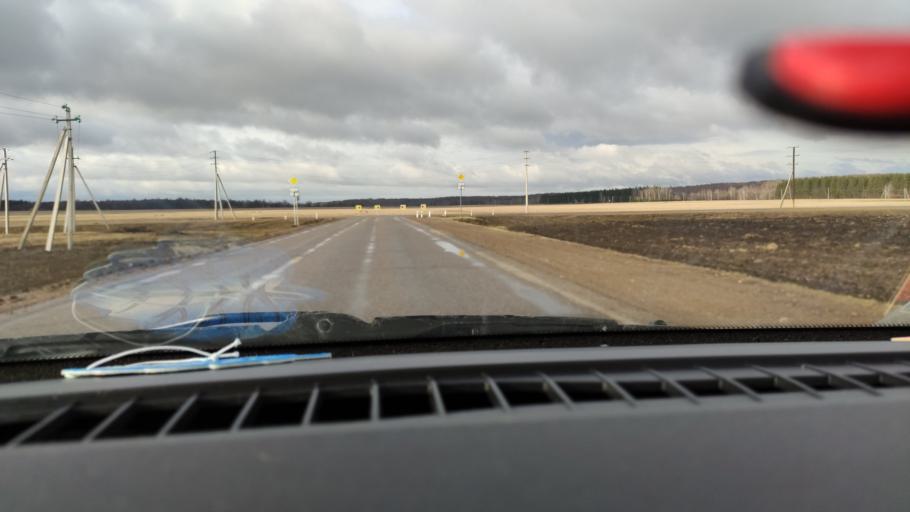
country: RU
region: Tatarstan
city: Russkiy Aktash
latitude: 55.0281
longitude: 51.8979
